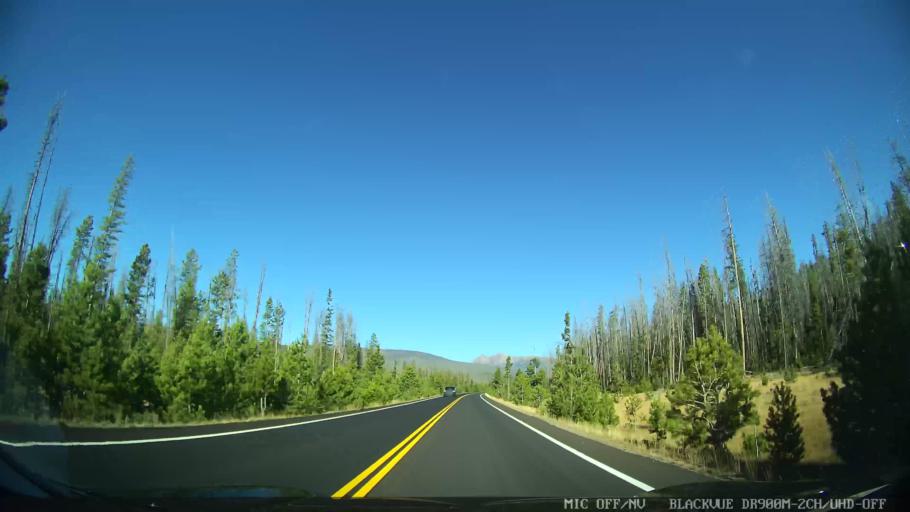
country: US
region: Colorado
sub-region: Grand County
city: Granby
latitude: 40.2827
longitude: -105.8387
